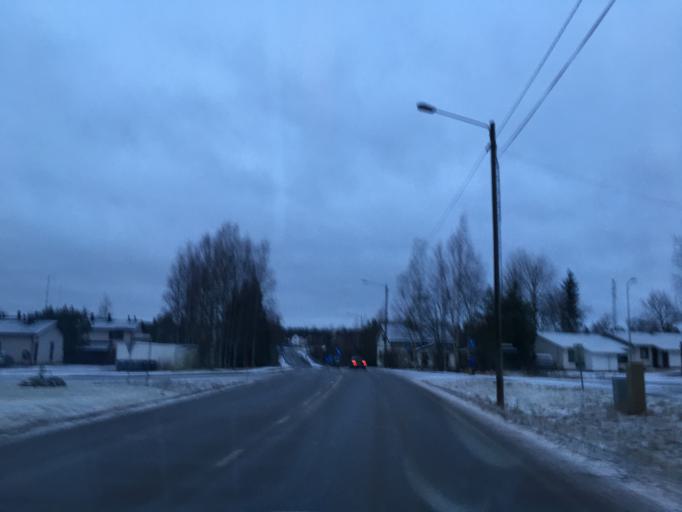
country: FI
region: Varsinais-Suomi
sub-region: Loimaa
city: Aura
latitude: 60.6462
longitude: 22.5981
